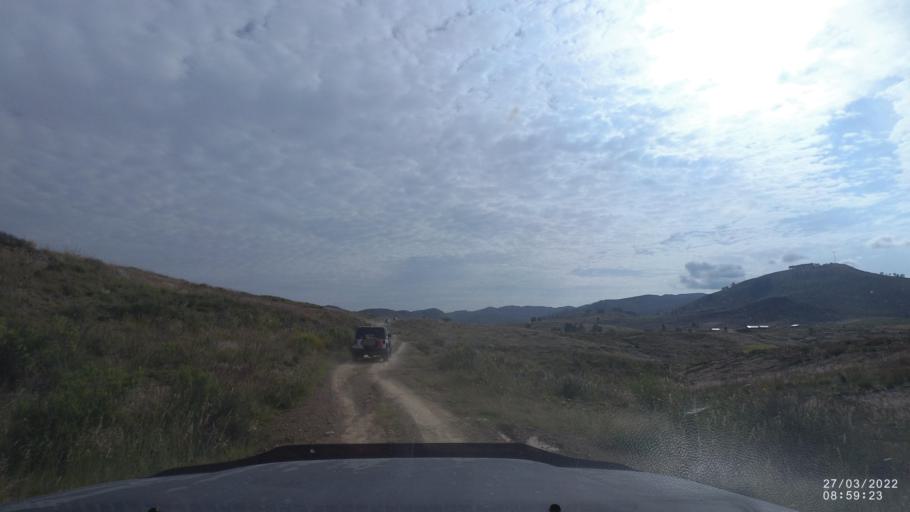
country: BO
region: Cochabamba
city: Cliza
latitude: -17.7396
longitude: -65.8547
